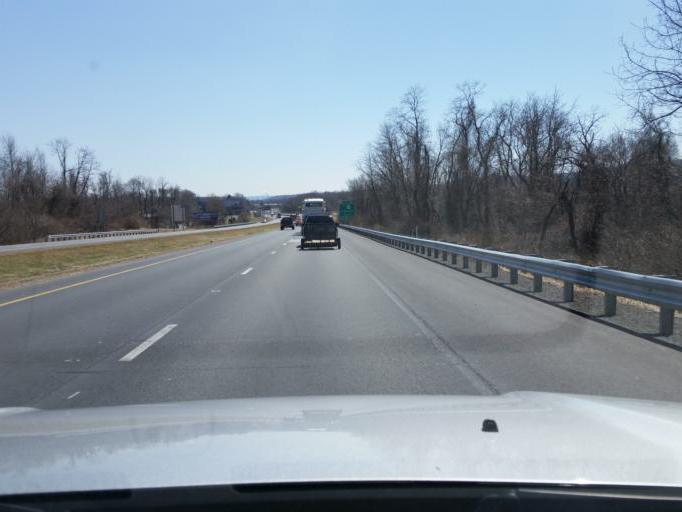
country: US
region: Pennsylvania
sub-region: Dauphin County
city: Highspire
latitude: 40.2289
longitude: -76.7944
